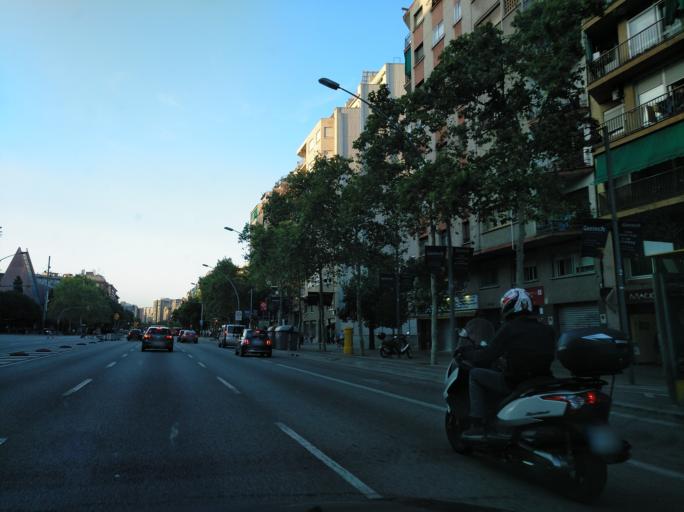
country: ES
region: Catalonia
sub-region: Provincia de Barcelona
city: Sant Marti
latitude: 41.4162
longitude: 2.1870
